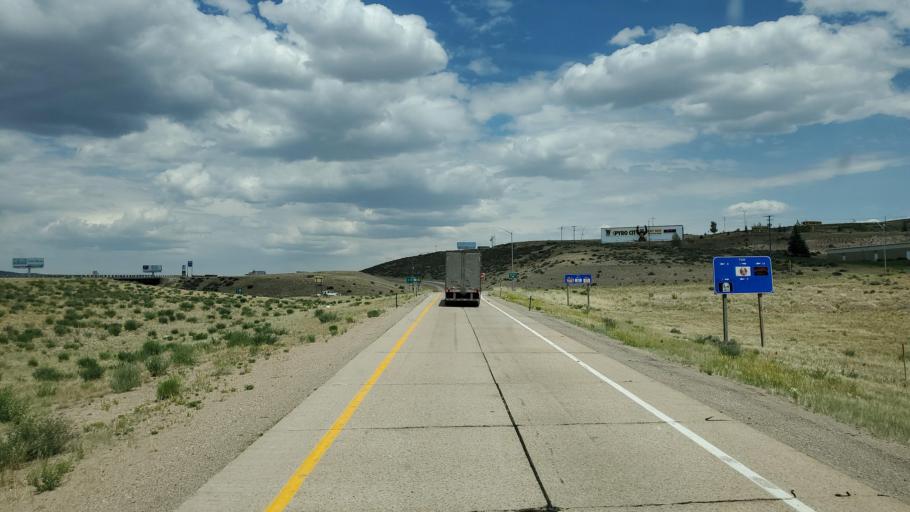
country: US
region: Wyoming
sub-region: Uinta County
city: Evanston
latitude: 41.2592
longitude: -110.9876
